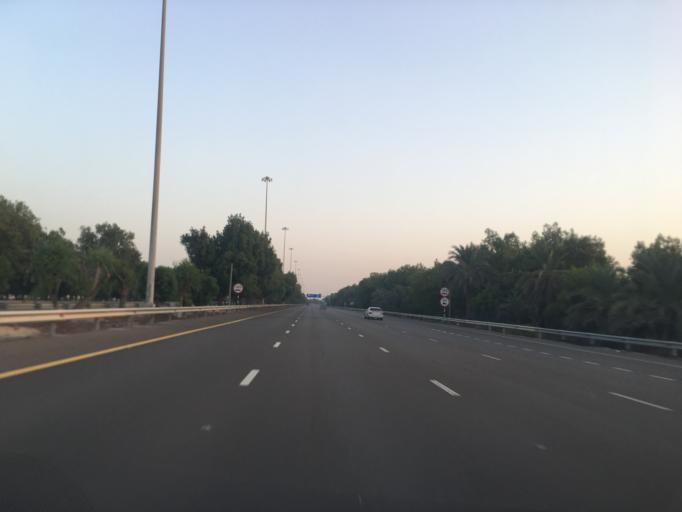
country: AE
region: Abu Dhabi
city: Abu Dhabi
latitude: 24.3398
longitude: 54.5774
